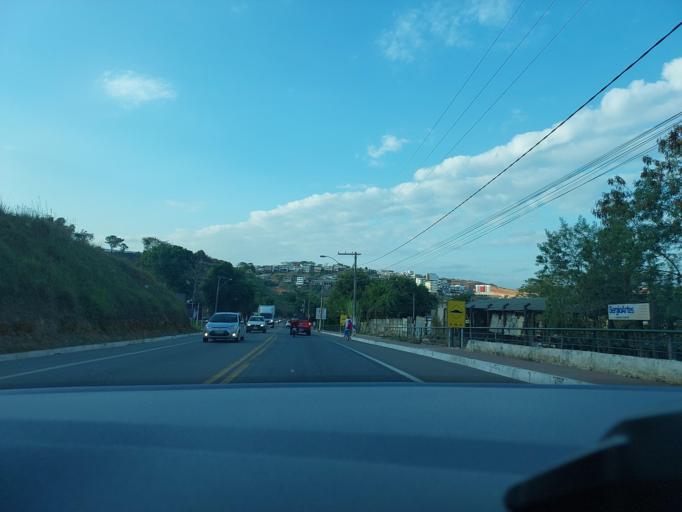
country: BR
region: Minas Gerais
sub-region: Muriae
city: Muriae
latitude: -21.1285
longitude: -42.3582
